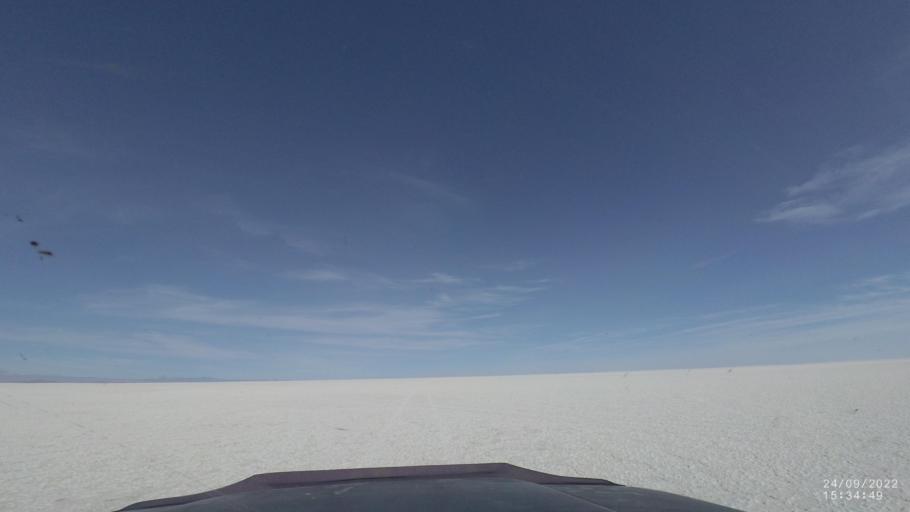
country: BO
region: Potosi
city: Colchani
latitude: -20.1284
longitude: -67.2593
